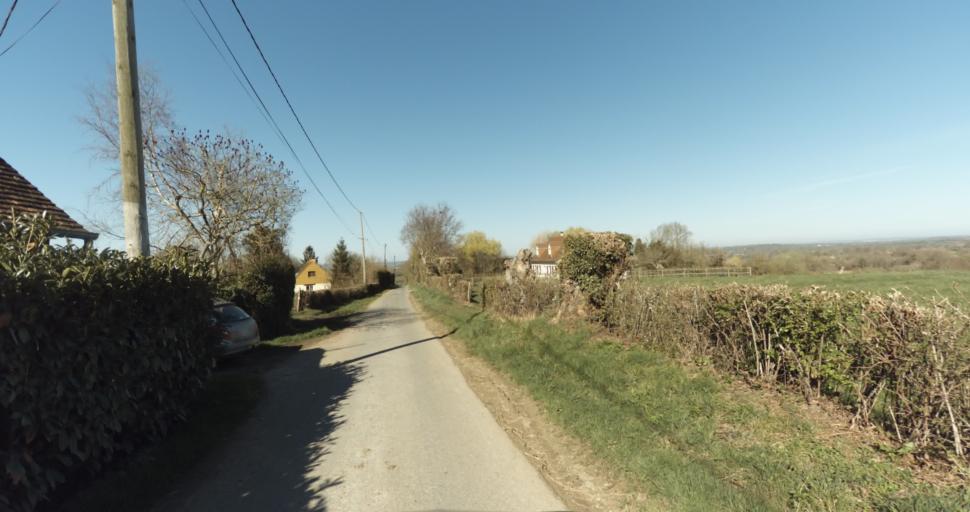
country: FR
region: Lower Normandy
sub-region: Departement de l'Orne
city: Trun
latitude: 48.9138
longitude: 0.0482
